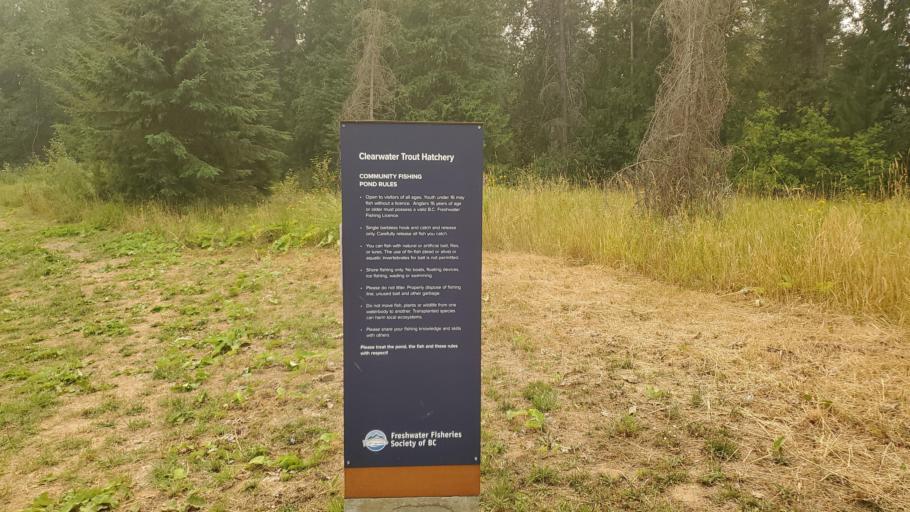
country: CA
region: British Columbia
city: Chase
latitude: 51.6471
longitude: -120.0638
